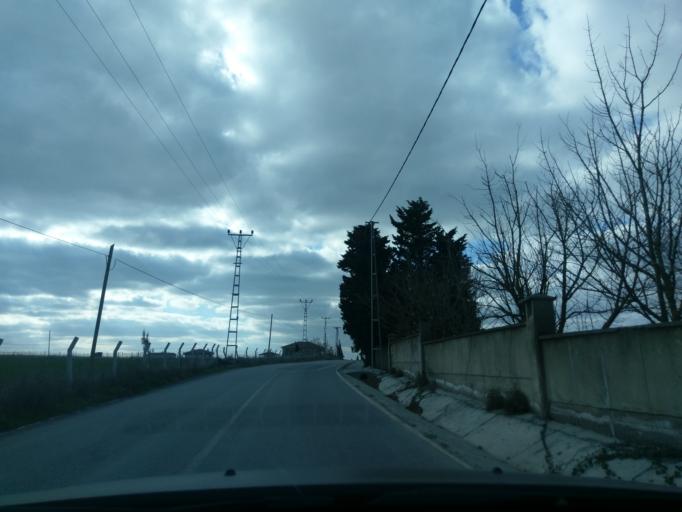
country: TR
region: Istanbul
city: Durusu
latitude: 41.3088
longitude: 28.6890
